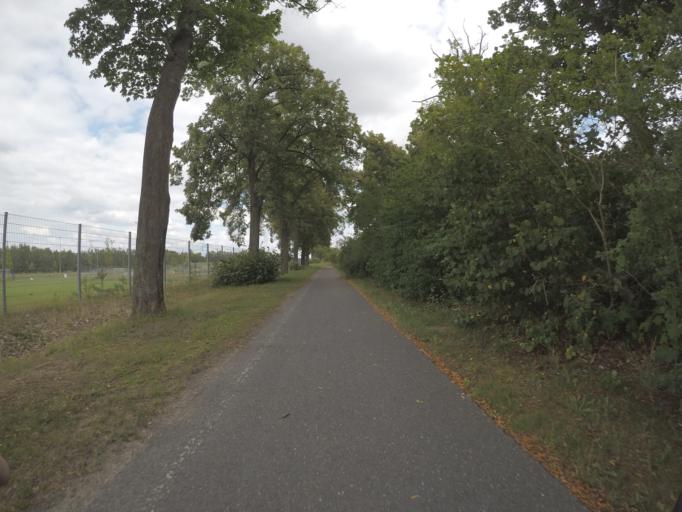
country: DE
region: Brandenburg
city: Dallgow-Doeberitz
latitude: 52.5348
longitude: 13.0691
